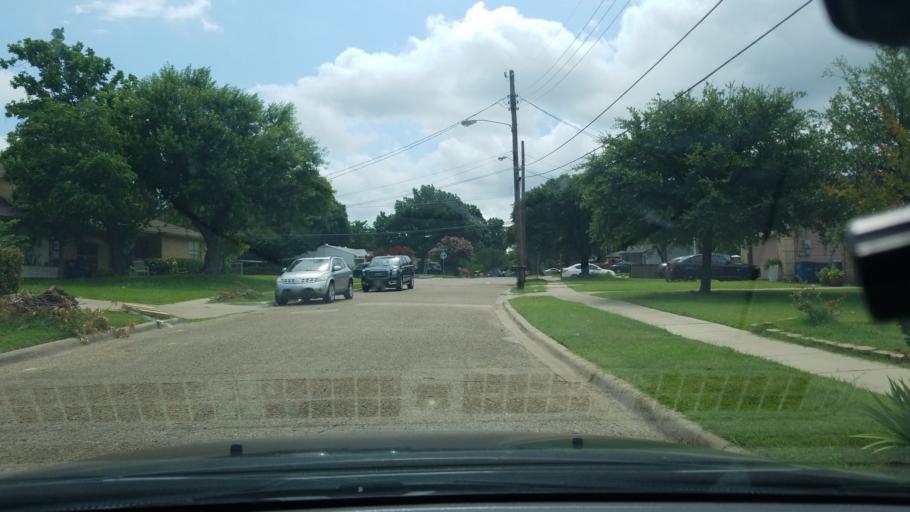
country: US
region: Texas
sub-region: Dallas County
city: Garland
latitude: 32.8240
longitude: -96.6784
